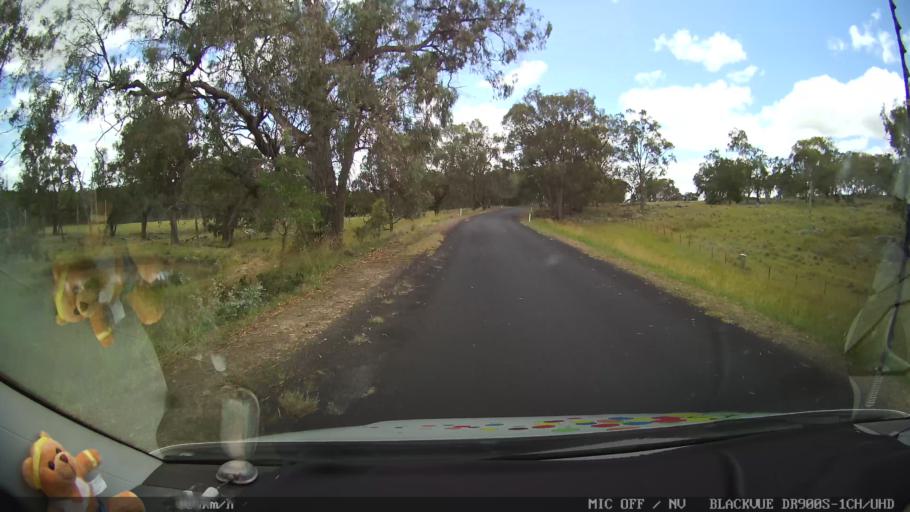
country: AU
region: New South Wales
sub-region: Glen Innes Severn
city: Glen Innes
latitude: -29.4287
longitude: 151.6606
